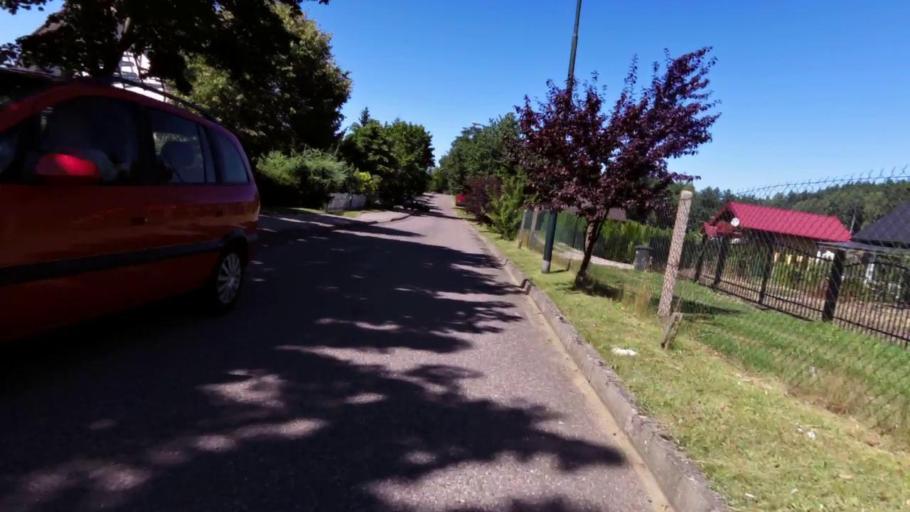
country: PL
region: West Pomeranian Voivodeship
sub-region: Powiat szczecinecki
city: Bialy Bor
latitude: 53.9019
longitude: 16.8310
